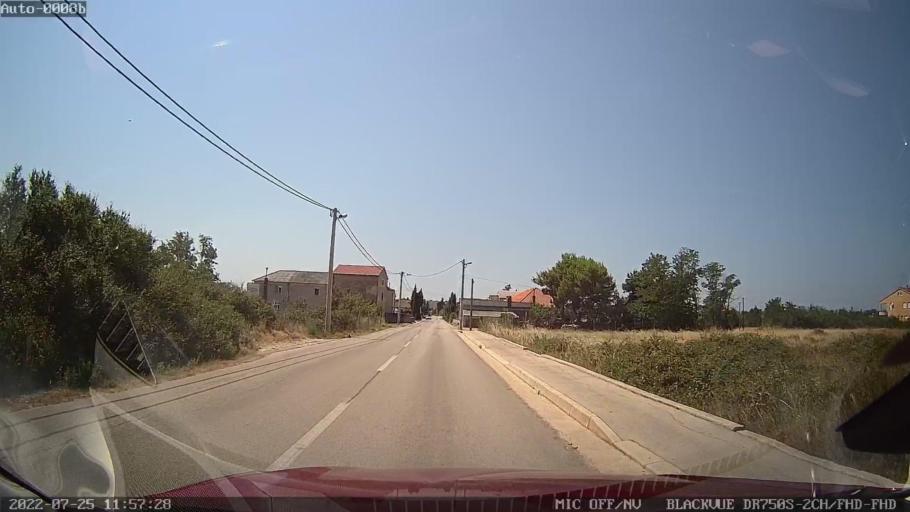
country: HR
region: Zadarska
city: Vrsi
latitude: 44.2430
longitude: 15.2142
